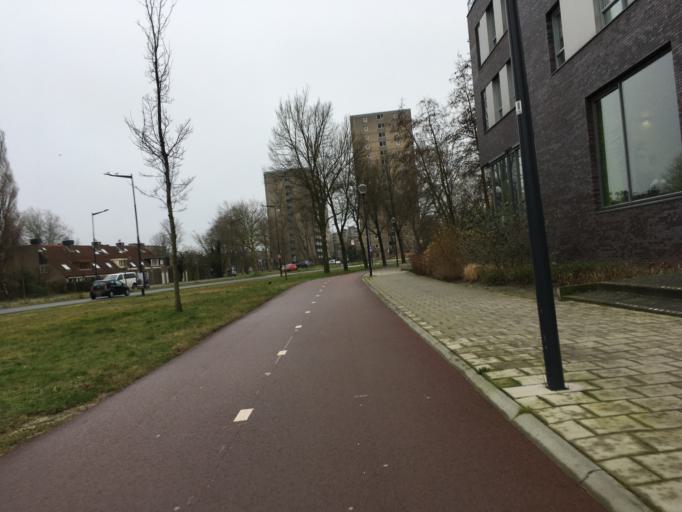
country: NL
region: North Holland
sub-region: Gemeente Haarlem
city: Haarlem
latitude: 52.3567
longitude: 4.6529
